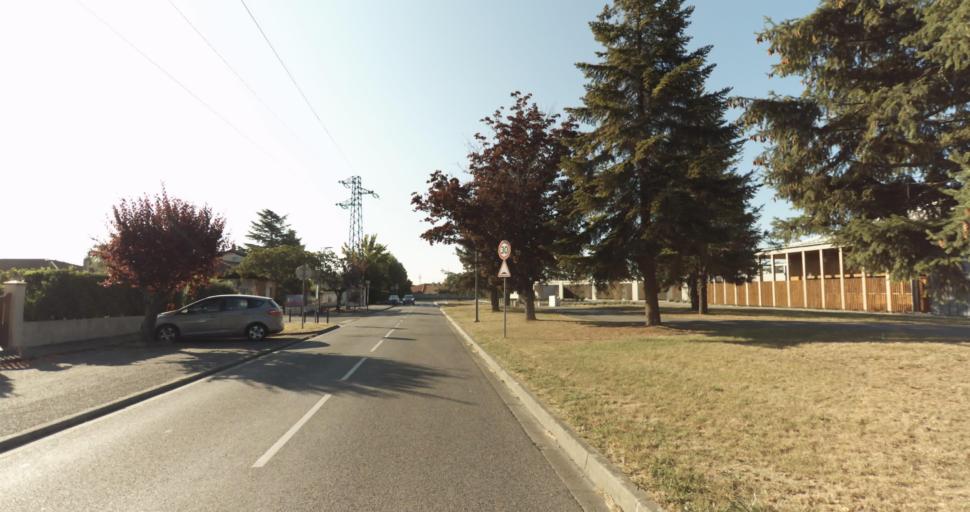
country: FR
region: Midi-Pyrenees
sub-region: Departement de la Haute-Garonne
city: L'Union
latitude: 43.6561
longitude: 1.4910
